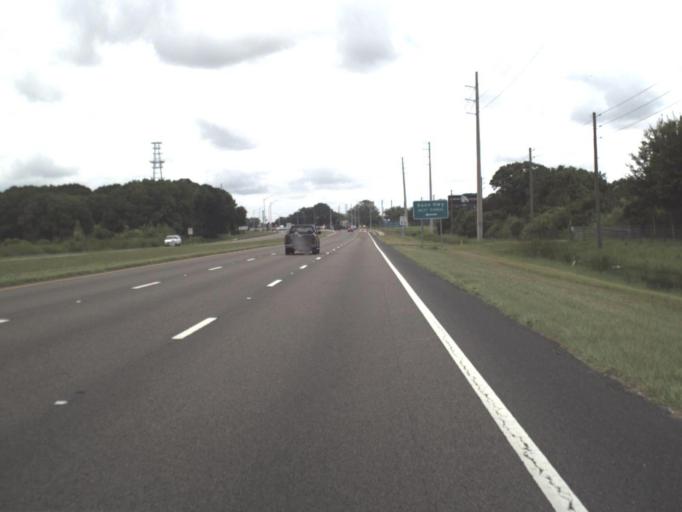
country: US
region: Florida
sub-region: Pasco County
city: Odessa
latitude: 28.1938
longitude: -82.5869
